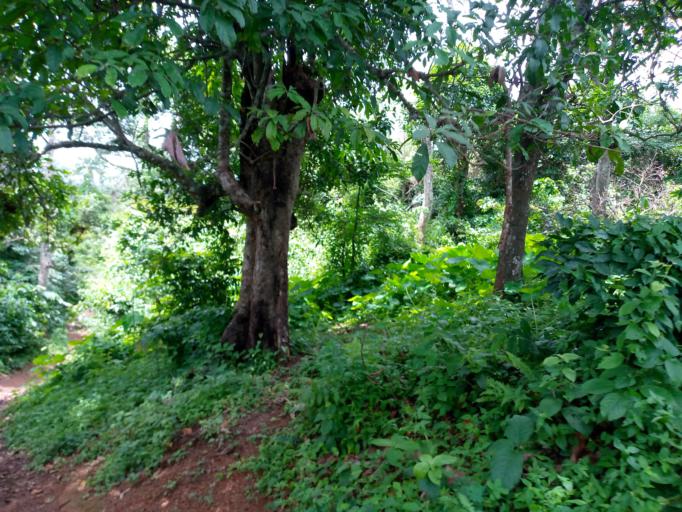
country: SL
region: Northern Province
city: Mange
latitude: 8.9796
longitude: -12.7481
